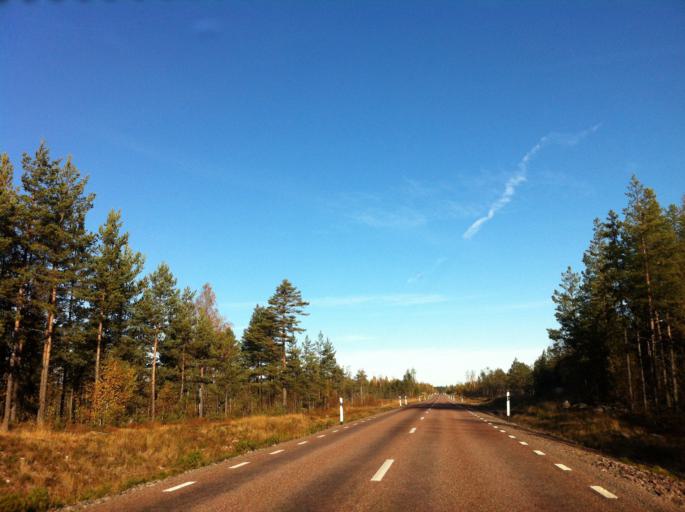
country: SE
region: Gaevleborg
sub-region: Gavle Kommun
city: Gavle
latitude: 60.5966
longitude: 17.1254
